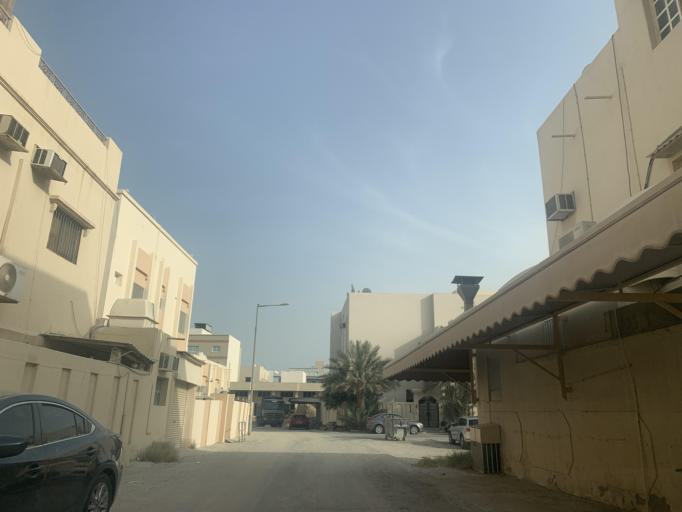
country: BH
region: Northern
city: Ar Rifa'
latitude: 26.1333
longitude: 50.5607
